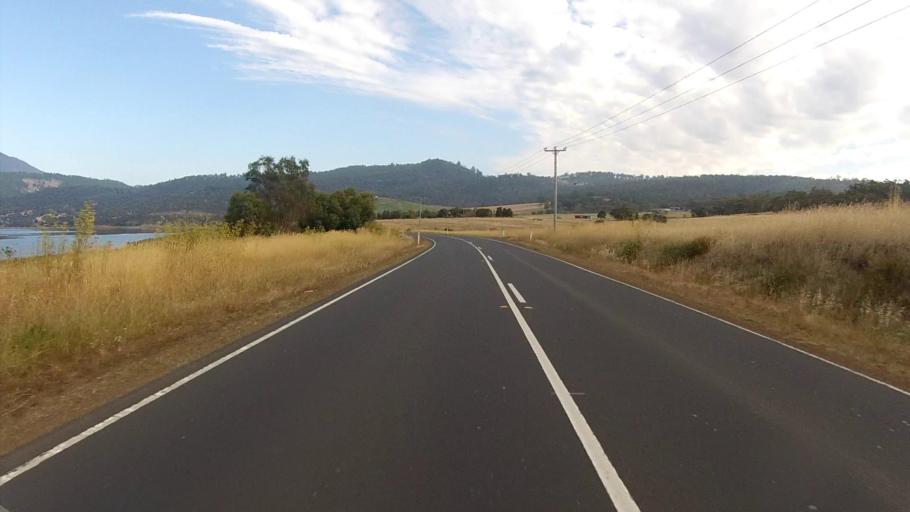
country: AU
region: Tasmania
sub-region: Brighton
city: Bridgewater
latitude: -42.7320
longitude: 147.2107
